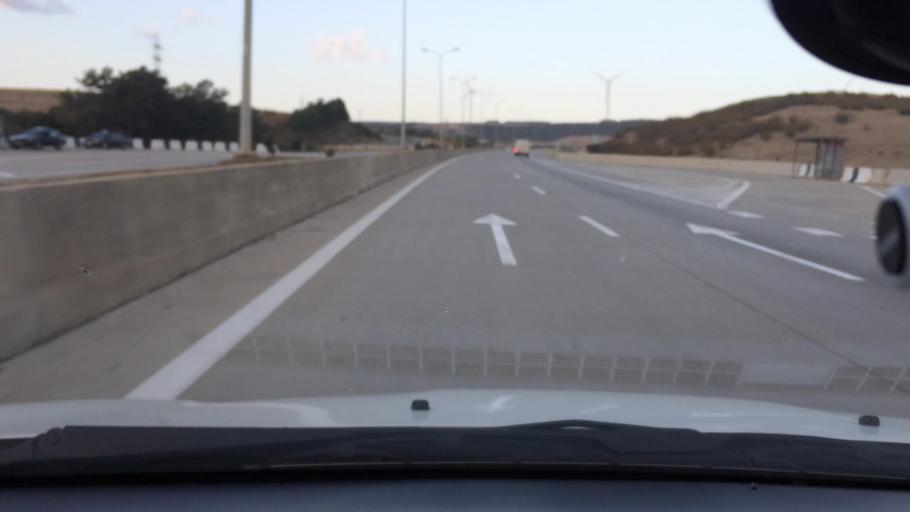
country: GE
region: Shida Kartli
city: Gori
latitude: 42.0156
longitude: 44.0758
